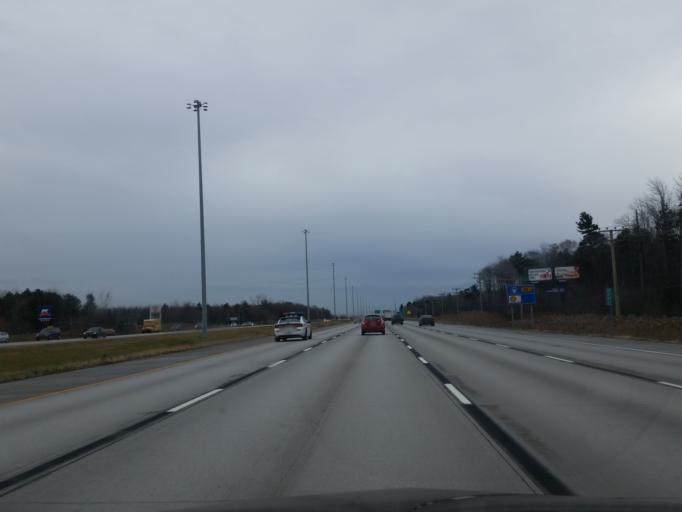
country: CA
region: Quebec
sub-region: Laurentides
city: Blainville
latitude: 45.6615
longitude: -73.8912
